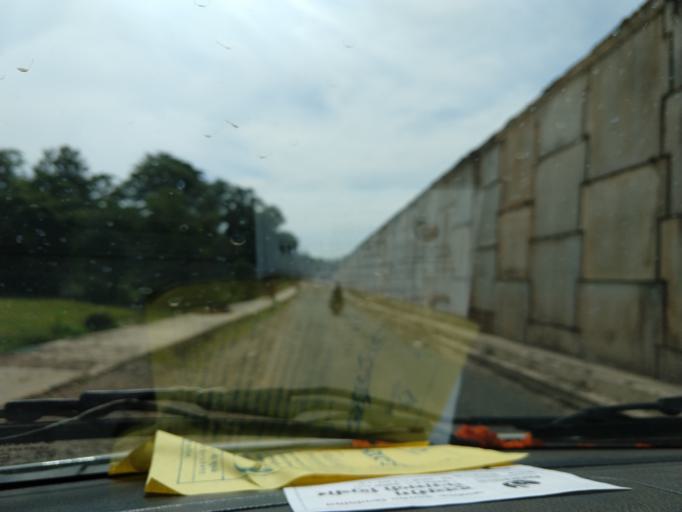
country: IN
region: Maharashtra
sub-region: Sindhudurg
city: Kudal
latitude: 15.9538
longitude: 73.7378
